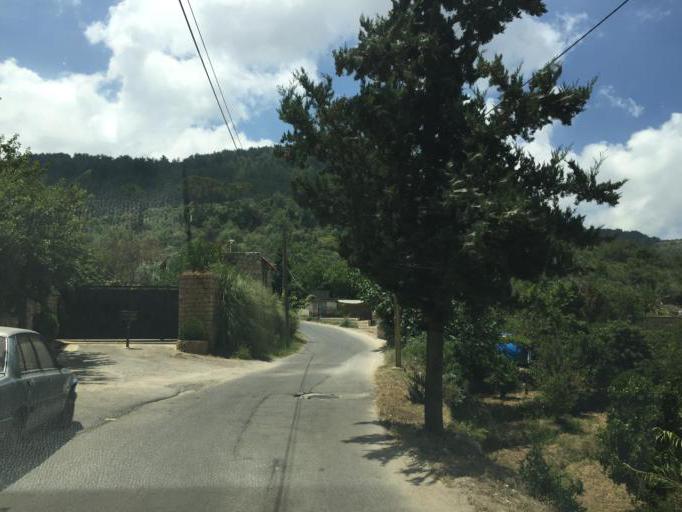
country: LB
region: Mont-Liban
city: Beit ed Dine
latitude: 33.6950
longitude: 35.5736
